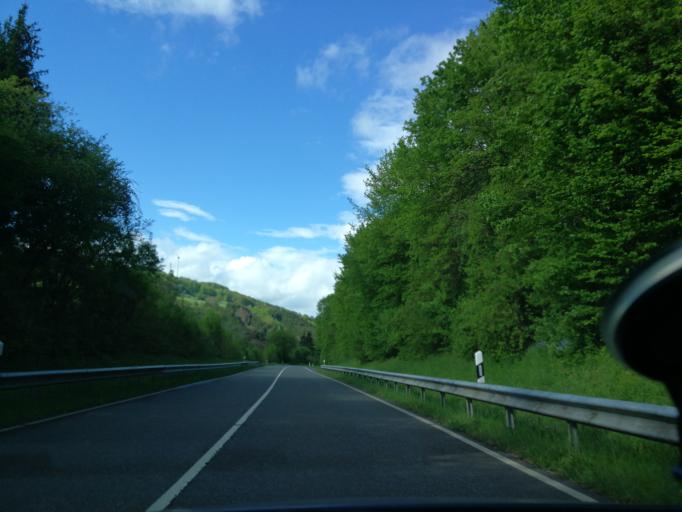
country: DE
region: Rheinland-Pfalz
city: Oberbillig
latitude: 49.7492
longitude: 6.5029
